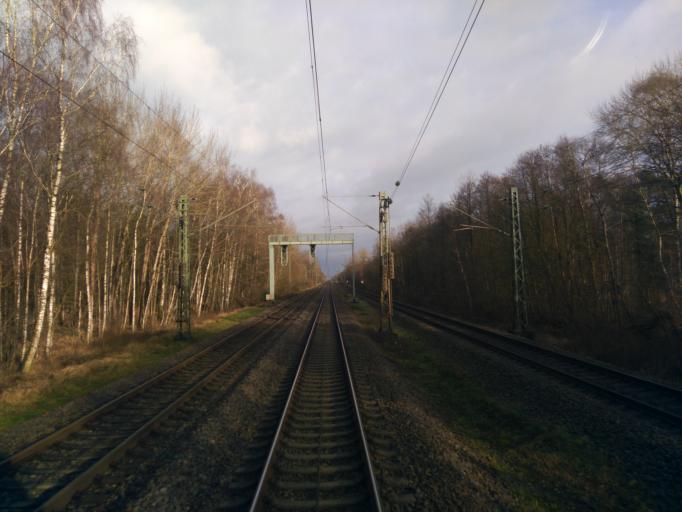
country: DE
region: Lower Saxony
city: Konigsmoor
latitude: 53.2377
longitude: 9.6578
